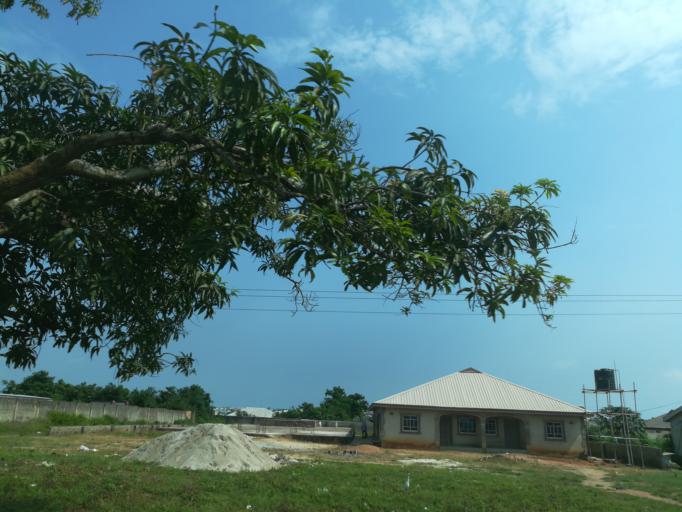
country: NG
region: Lagos
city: Ikorodu
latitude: 6.6059
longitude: 3.6264
